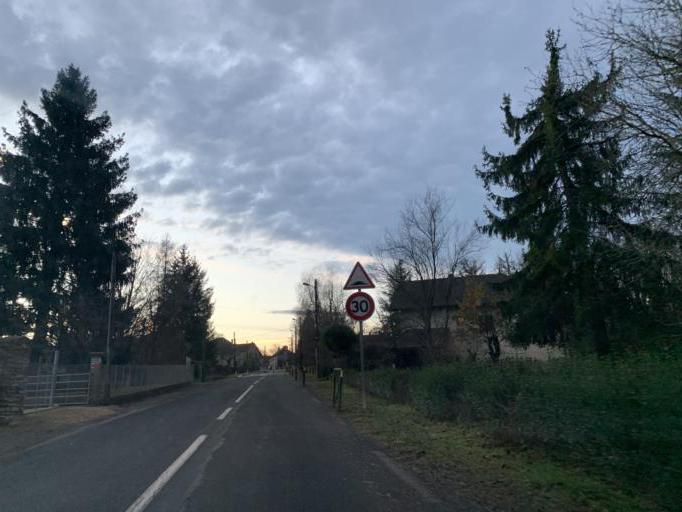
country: FR
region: Rhone-Alpes
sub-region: Departement de l'Ain
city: Virieu-le-Grand
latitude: 45.8079
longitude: 5.6243
